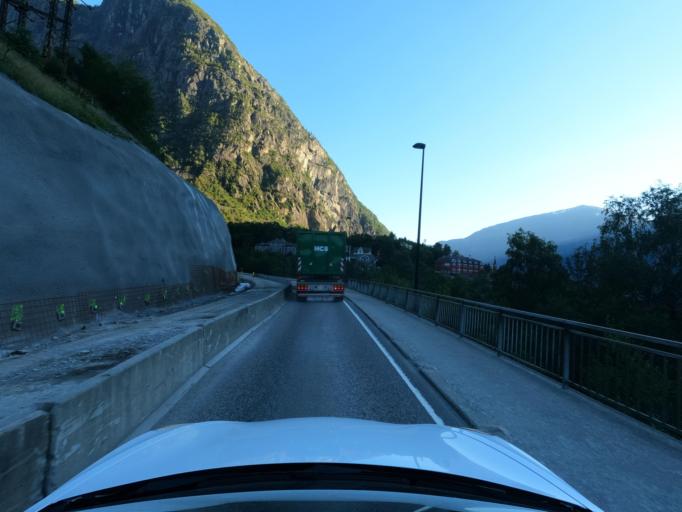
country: NO
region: Hordaland
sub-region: Odda
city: Odda
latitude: 60.1182
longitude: 6.5580
